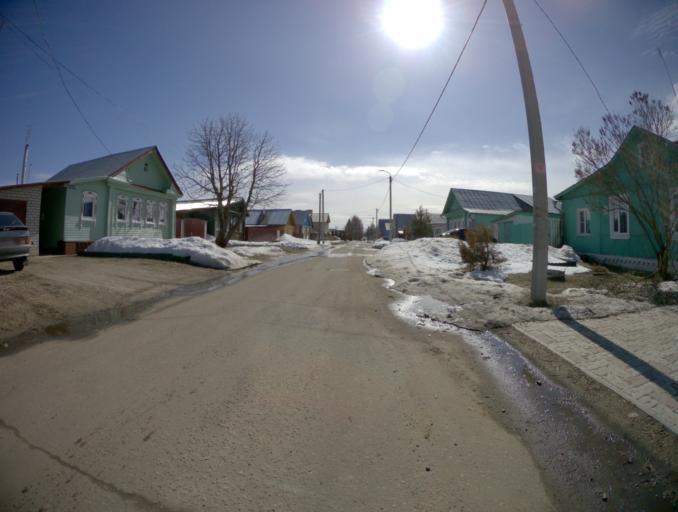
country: RU
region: Vladimir
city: Suzdal'
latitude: 56.4302
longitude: 40.4337
